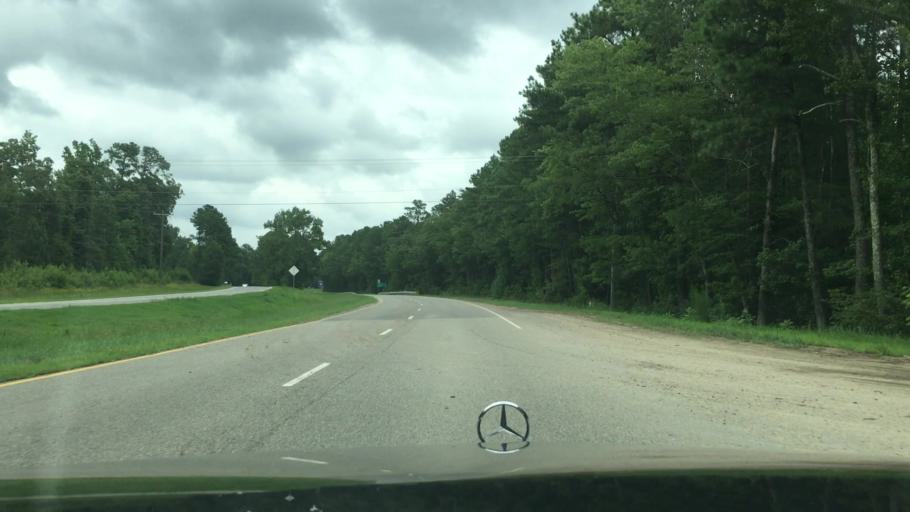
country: US
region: Virginia
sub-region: Chesterfield County
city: Woodlake
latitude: 37.3932
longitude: -77.7888
